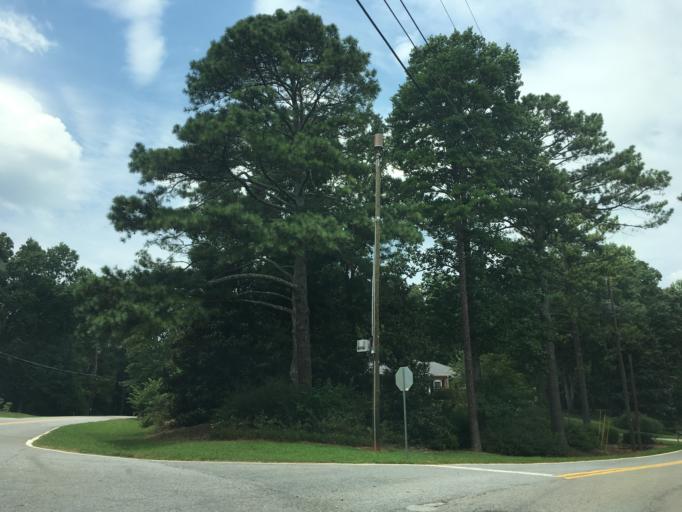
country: US
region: Georgia
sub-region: Fulton County
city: Alpharetta
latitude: 34.0876
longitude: -84.3347
